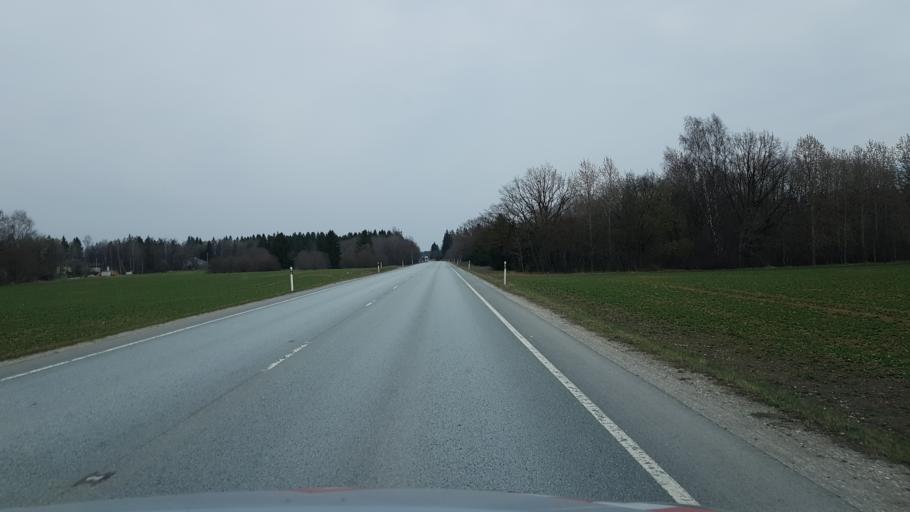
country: EE
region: Laeaene-Virumaa
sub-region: Rakvere linn
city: Rakvere
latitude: 59.3221
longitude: 26.3784
